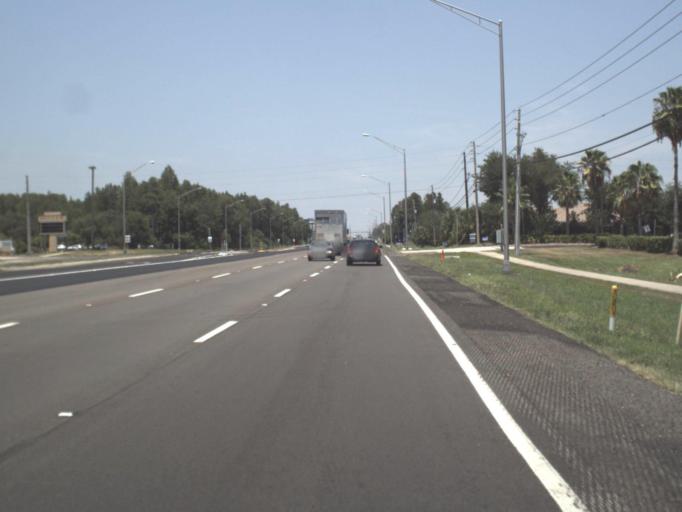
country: US
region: Florida
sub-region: Pinellas County
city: Tarpon Springs
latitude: 28.1142
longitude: -82.7397
